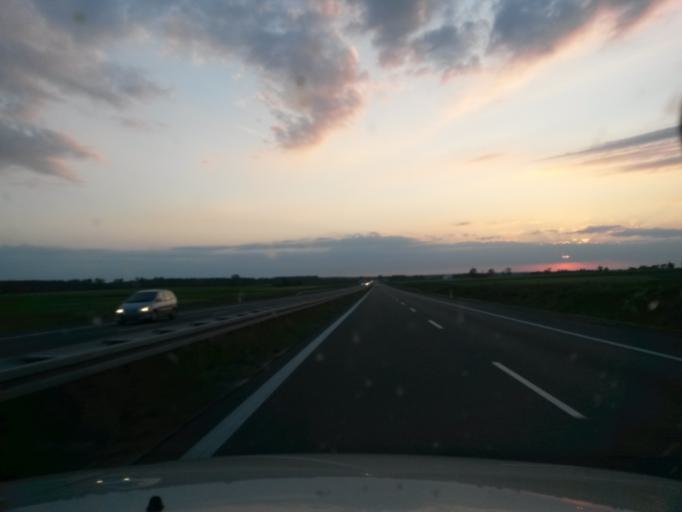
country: PL
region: Lower Silesian Voivodeship
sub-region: Powiat olesnicki
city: Sycow
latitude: 51.2998
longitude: 17.6503
